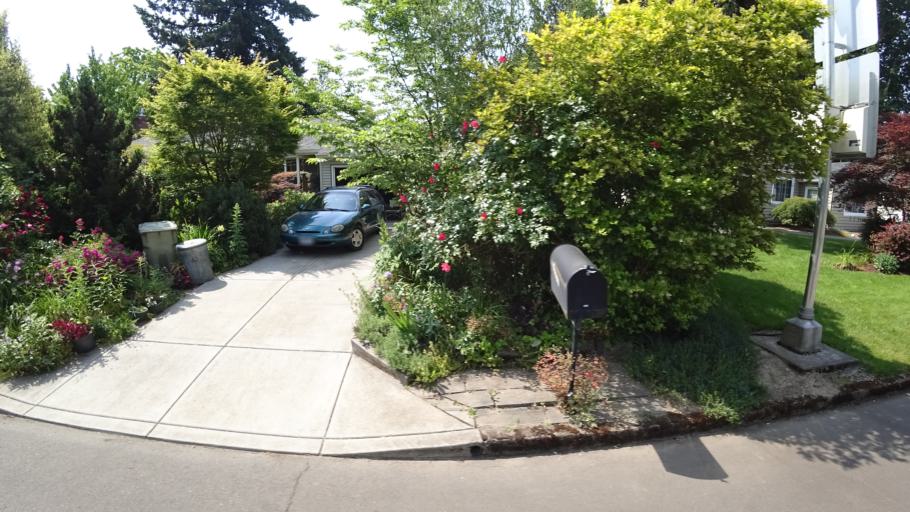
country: US
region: Oregon
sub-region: Washington County
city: Cedar Mill
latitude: 45.5208
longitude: -122.8186
